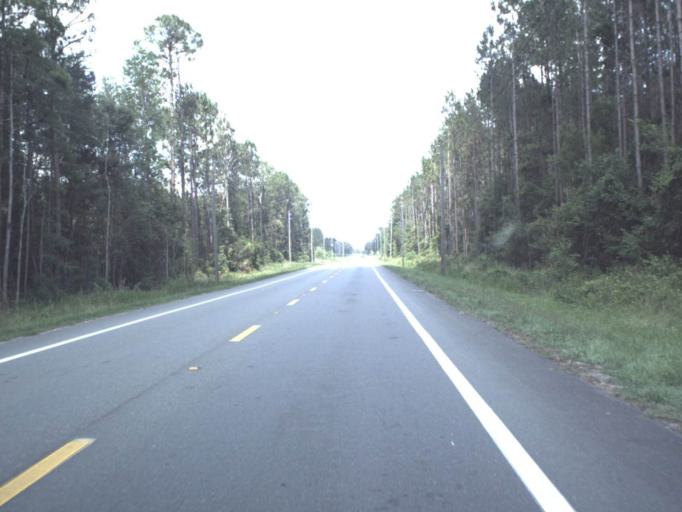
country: US
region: Florida
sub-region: Baker County
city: Macclenny
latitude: 30.2877
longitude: -82.0906
